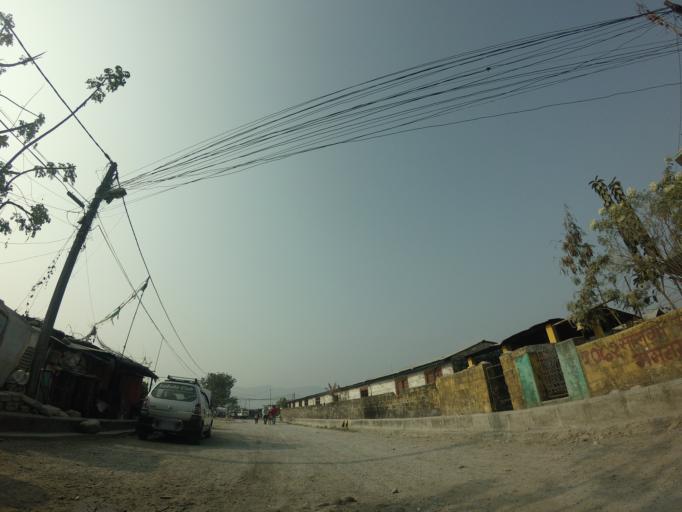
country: NP
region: Western Region
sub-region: Gandaki Zone
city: Pokhara
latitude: 28.2068
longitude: 83.9883
